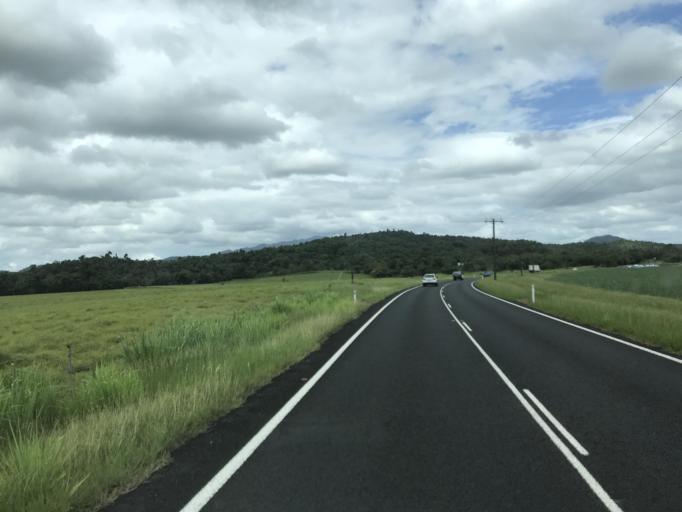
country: AU
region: Queensland
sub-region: Cassowary Coast
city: Innisfail
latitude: -17.8254
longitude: 146.0490
